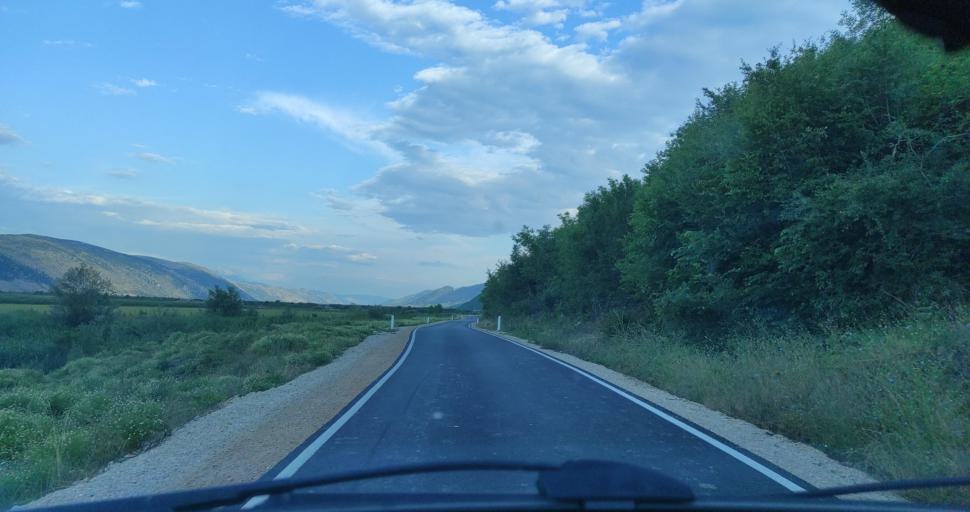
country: AL
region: Shkoder
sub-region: Rrethi i Shkodres
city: Velipoje
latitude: 41.9262
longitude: 19.4484
